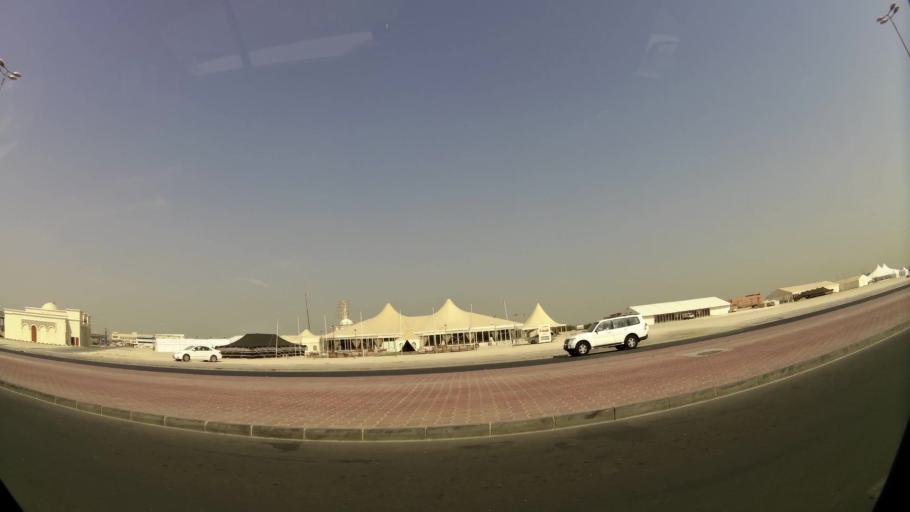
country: KW
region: Al Asimah
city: Ar Rabiyah
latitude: 29.2793
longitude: 47.9173
